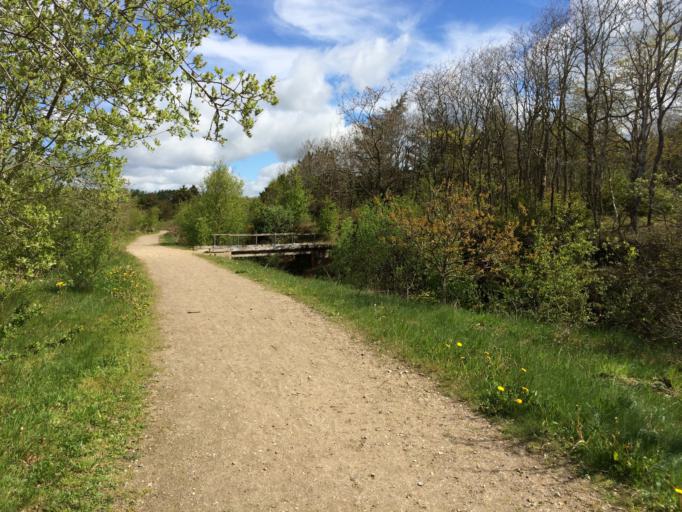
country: DK
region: Central Jutland
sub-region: Holstebro Kommune
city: Holstebro
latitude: 56.2251
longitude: 8.6185
